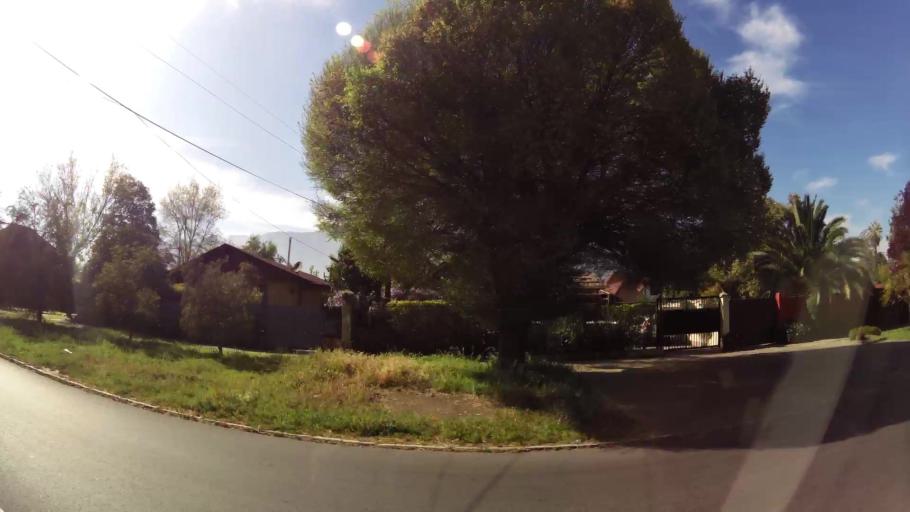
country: CL
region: Santiago Metropolitan
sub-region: Provincia de Santiago
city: Villa Presidente Frei, Nunoa, Santiago, Chile
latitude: -33.4504
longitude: -70.5574
